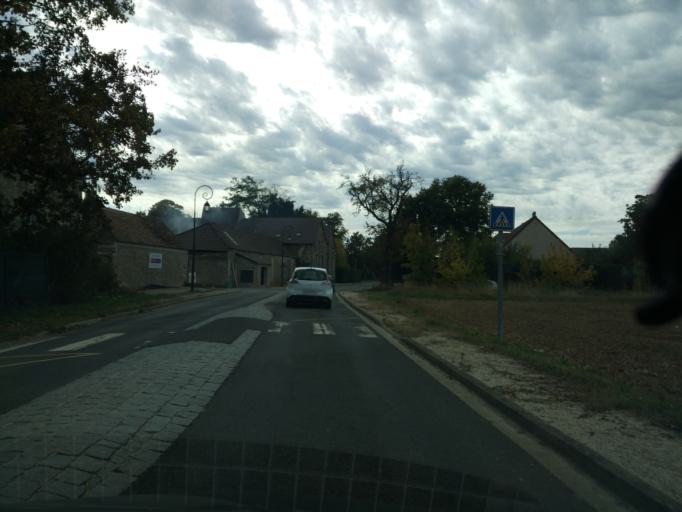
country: FR
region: Ile-de-France
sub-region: Departement de l'Essonne
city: Gometz-la-Ville
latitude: 48.6489
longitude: 2.1207
